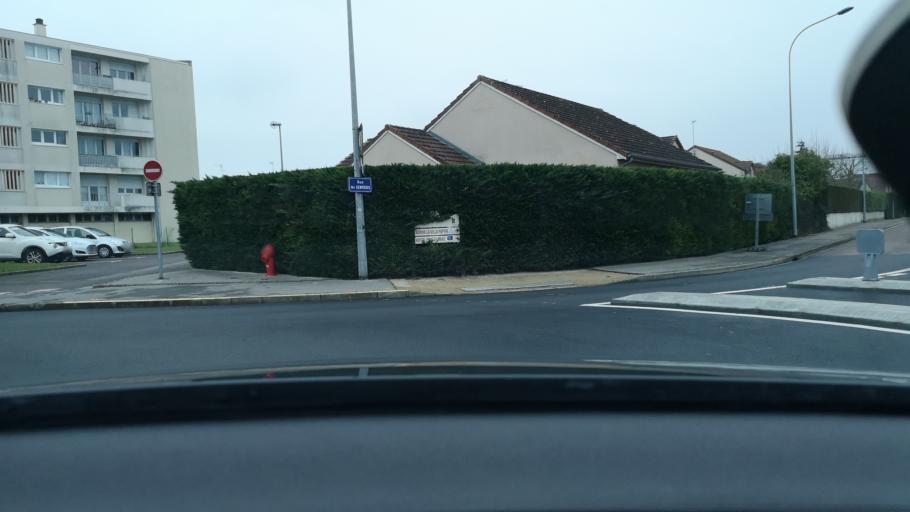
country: FR
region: Bourgogne
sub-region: Departement de Saone-et-Loire
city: Chalon-sur-Saone
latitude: 46.7997
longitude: 4.8564
